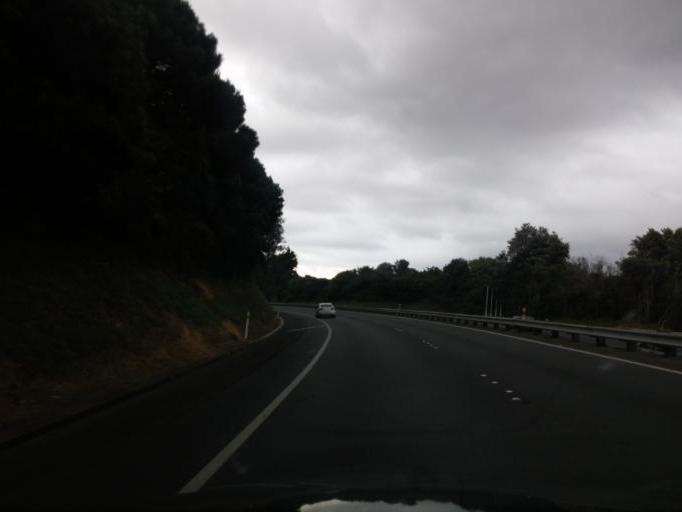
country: NZ
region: Wellington
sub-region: Porirua City
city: Porirua
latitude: -41.1801
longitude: 174.8288
